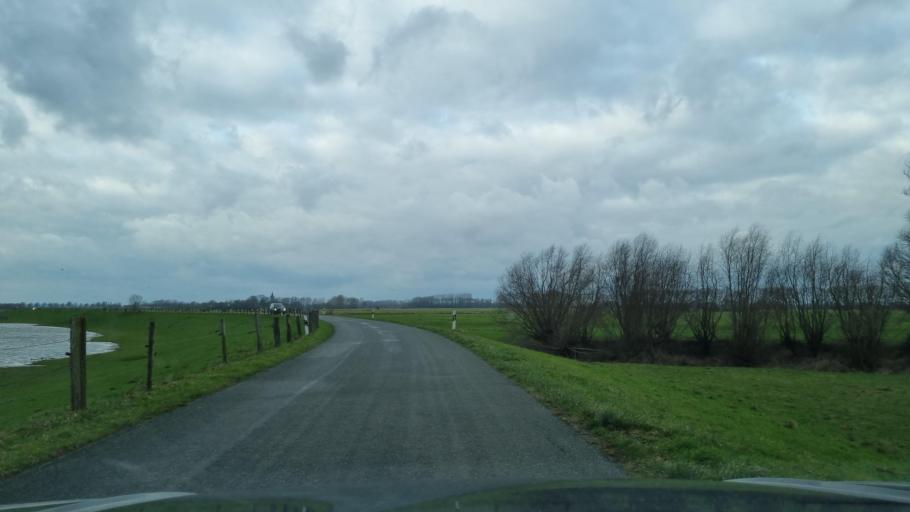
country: DE
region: North Rhine-Westphalia
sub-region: Regierungsbezirk Dusseldorf
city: Kleve
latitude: 51.8334
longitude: 6.1302
